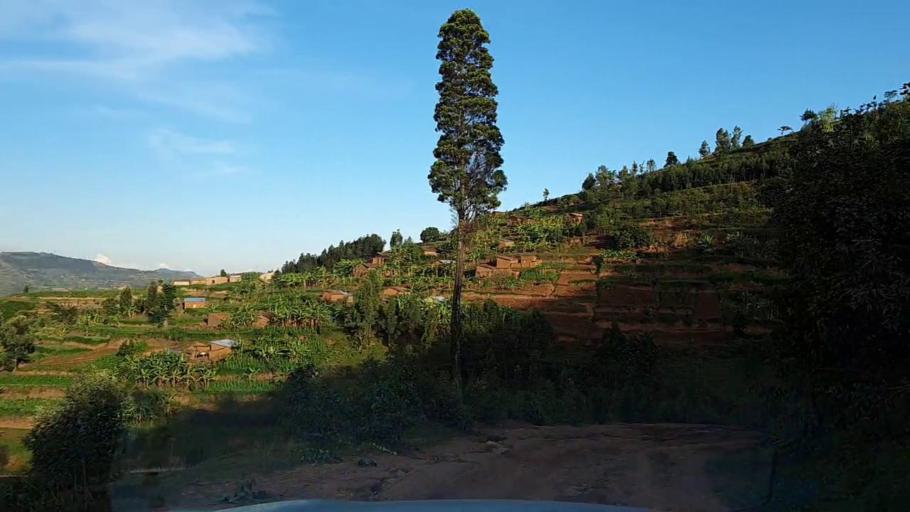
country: RW
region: Southern Province
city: Gikongoro
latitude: -2.4036
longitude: 29.5541
